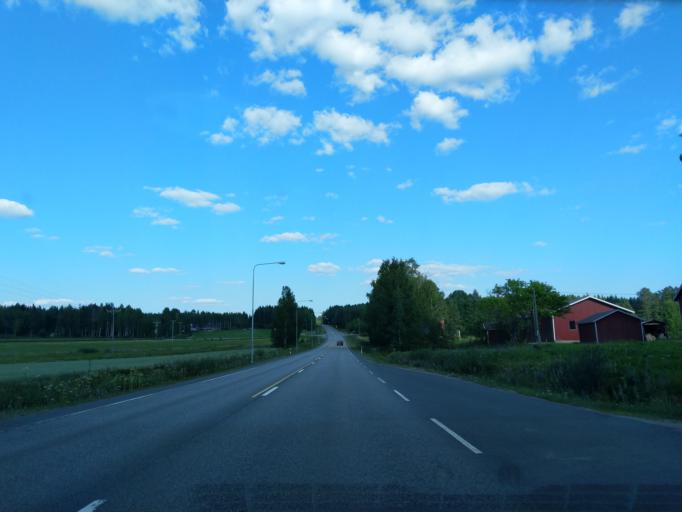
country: FI
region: Pirkanmaa
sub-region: Luoteis-Pirkanmaa
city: Kihnioe
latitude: 62.1987
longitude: 23.1833
